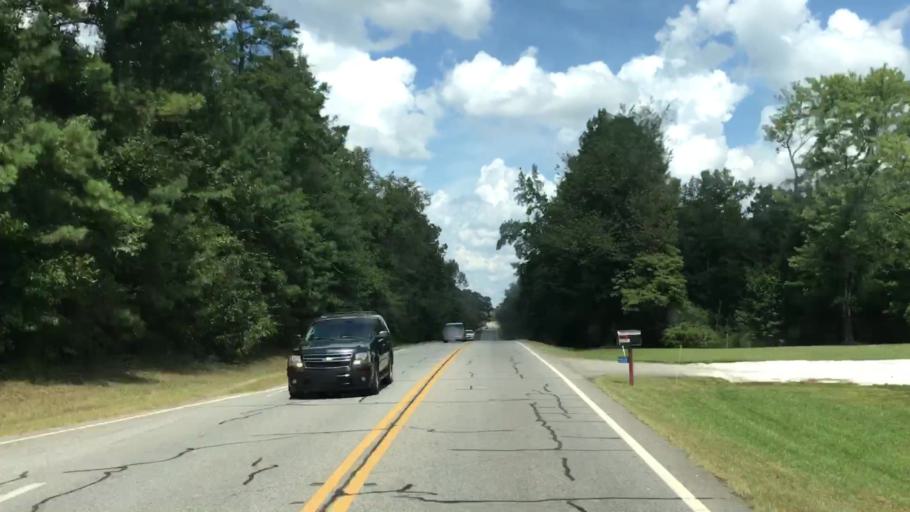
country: US
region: Georgia
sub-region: Oconee County
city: Watkinsville
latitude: 33.7703
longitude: -83.3102
